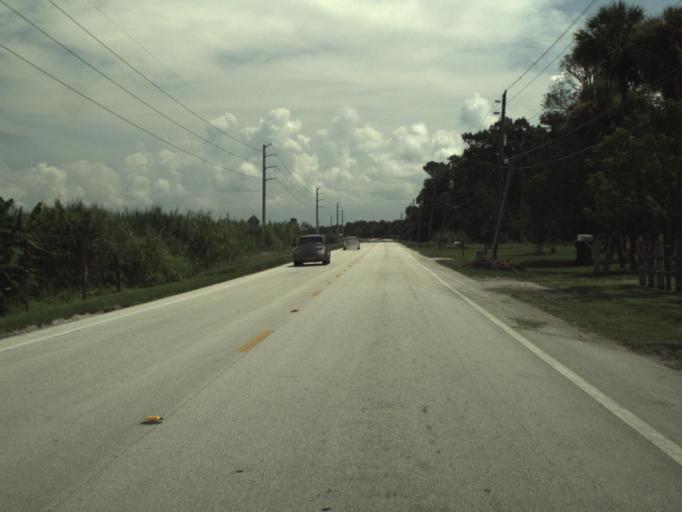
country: US
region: Florida
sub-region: Palm Beach County
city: Pahokee
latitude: 26.8741
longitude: -80.6237
